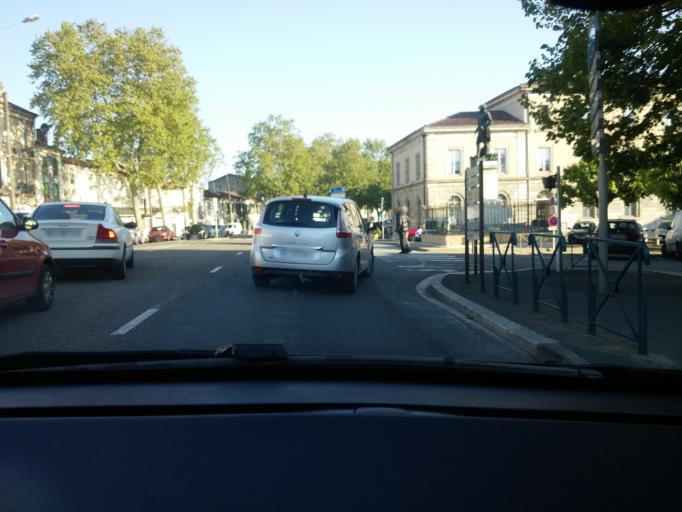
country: FR
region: Aquitaine
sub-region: Departement du Lot-et-Garonne
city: Nerac
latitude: 44.1353
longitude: 0.3369
